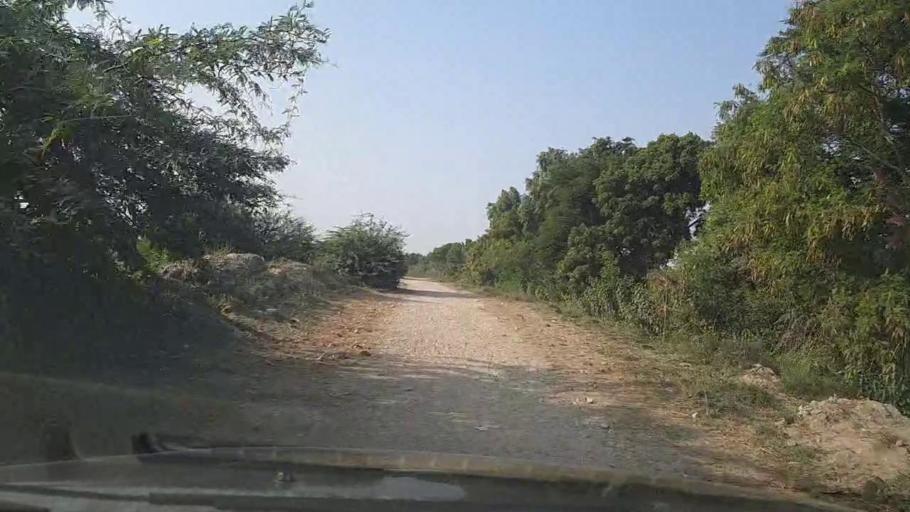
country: PK
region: Sindh
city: Mirpur Sakro
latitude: 24.6371
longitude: 67.7509
